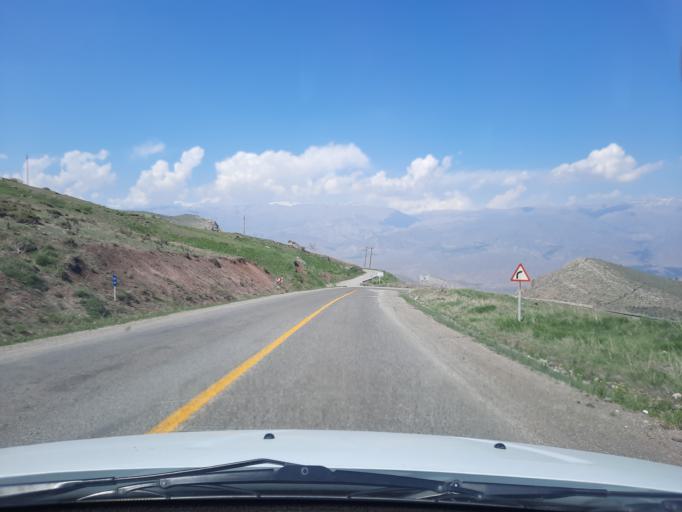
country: IR
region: Qazvin
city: Qazvin
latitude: 36.4062
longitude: 50.2253
